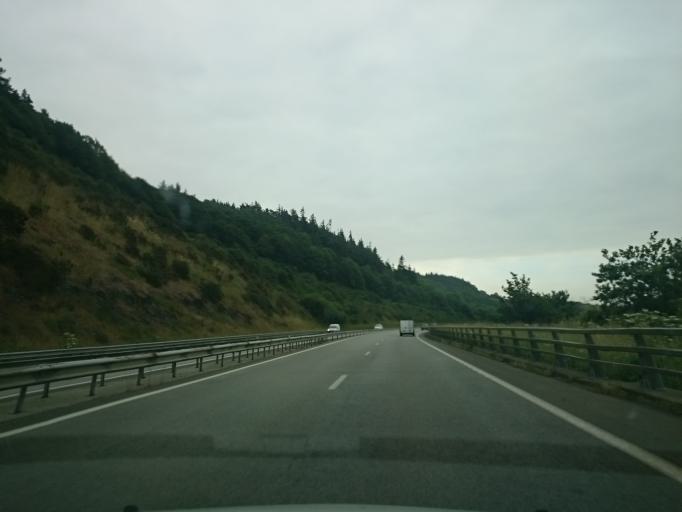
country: FR
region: Brittany
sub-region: Departement du Finistere
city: Chateaulin
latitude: 48.2465
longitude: -4.1089
